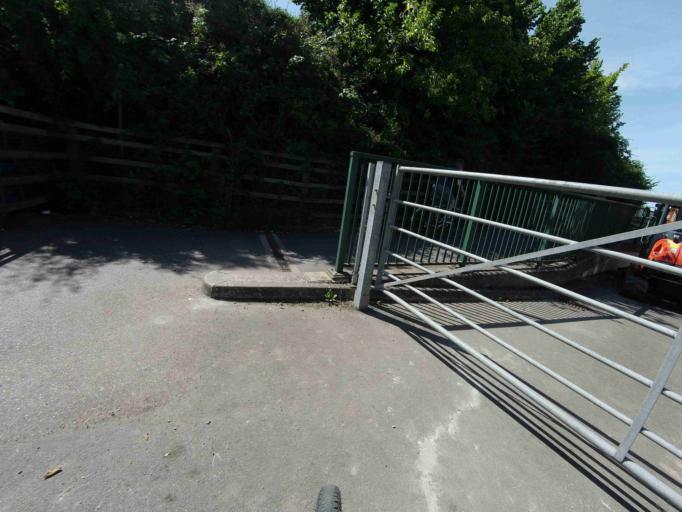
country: GB
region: England
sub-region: Devon
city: Starcross
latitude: 50.6486
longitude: -3.4314
